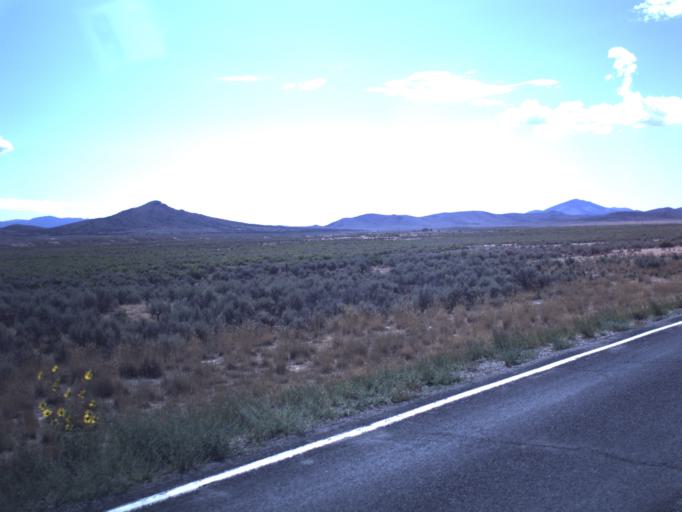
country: US
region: Utah
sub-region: Tooele County
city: Tooele
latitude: 40.1315
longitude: -112.4308
